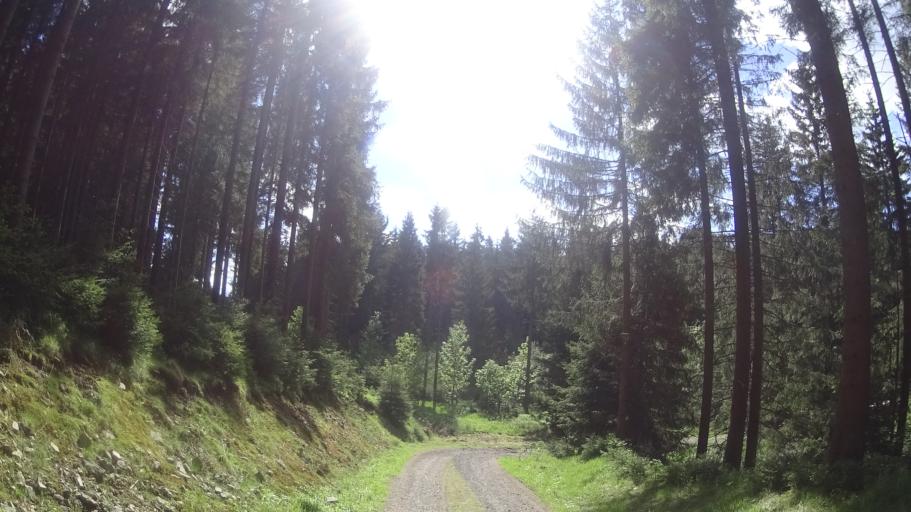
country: DE
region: Thuringia
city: Neustadt am Rennsteig
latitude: 50.6008
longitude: 10.9393
